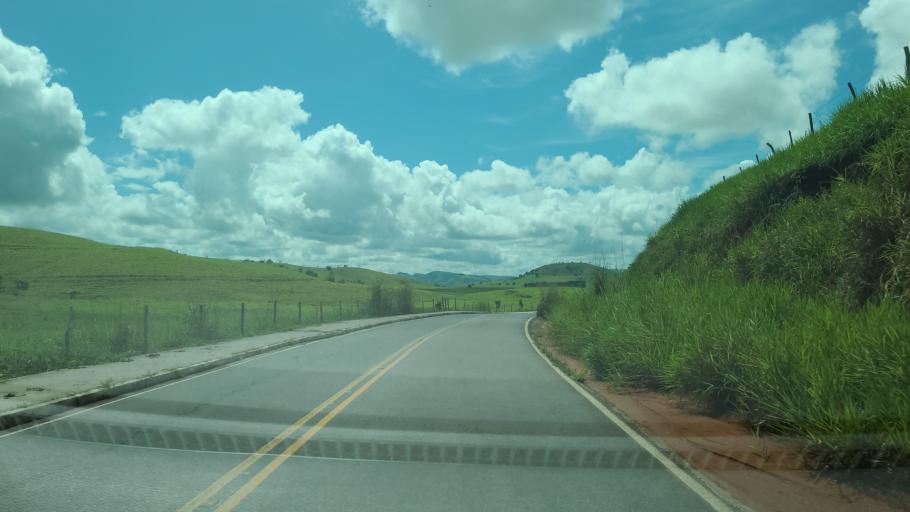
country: BR
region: Alagoas
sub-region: Uniao Dos Palmares
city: Uniao dos Palmares
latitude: -9.1652
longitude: -36.0554
